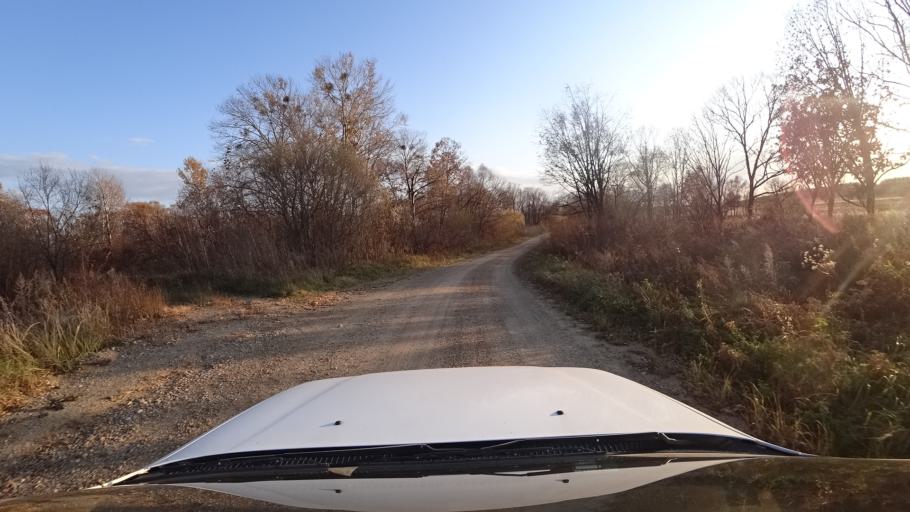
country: RU
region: Primorskiy
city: Lazo
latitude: 45.8163
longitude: 133.6112
